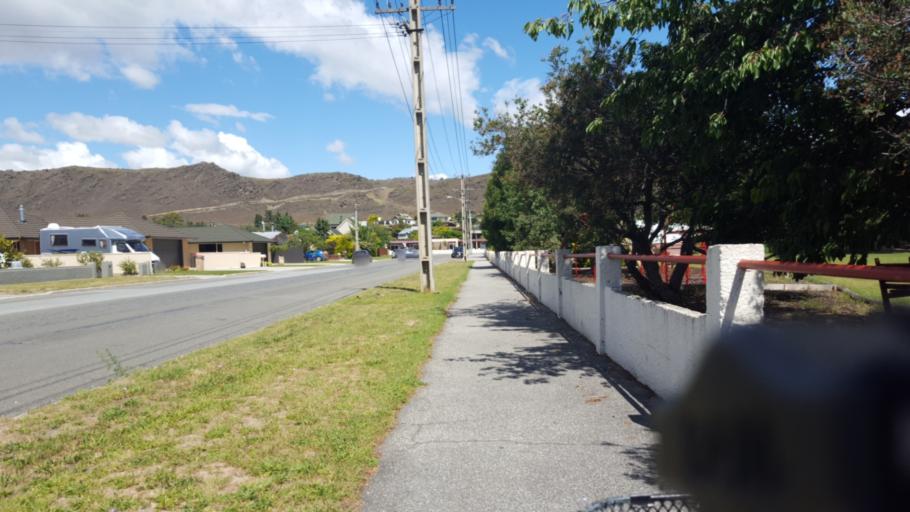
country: NZ
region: Otago
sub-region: Queenstown-Lakes District
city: Wanaka
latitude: -45.2485
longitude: 169.3961
